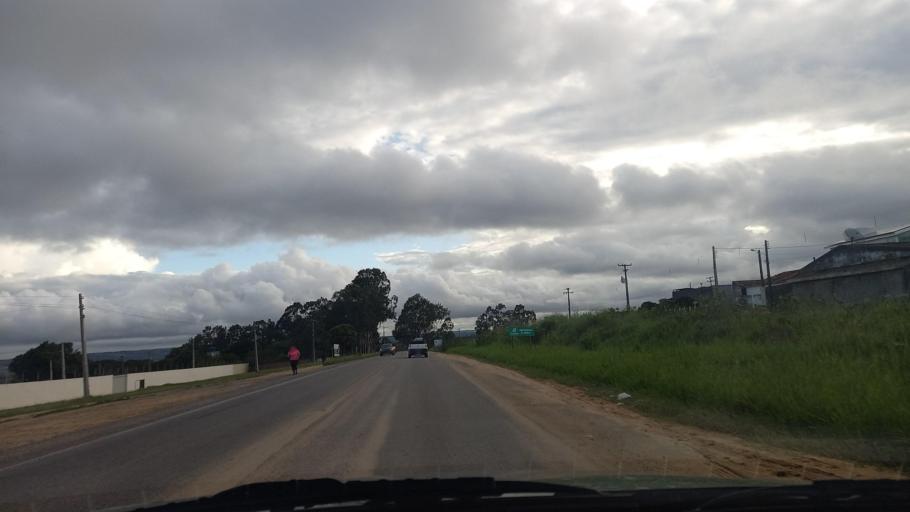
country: BR
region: Pernambuco
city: Garanhuns
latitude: -8.9101
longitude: -36.4912
